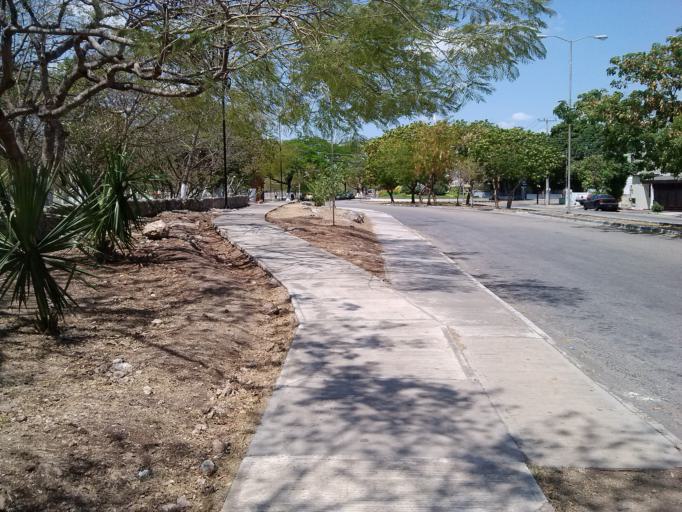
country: MX
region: Yucatan
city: Merida
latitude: 20.9698
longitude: -89.5845
